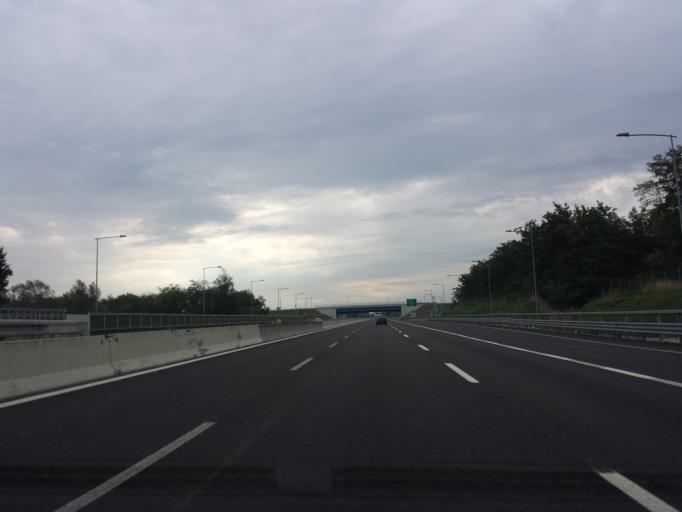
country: IT
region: Lombardy
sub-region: Provincia di Varese
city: Cassano Magnago
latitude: 45.6496
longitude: 8.8342
